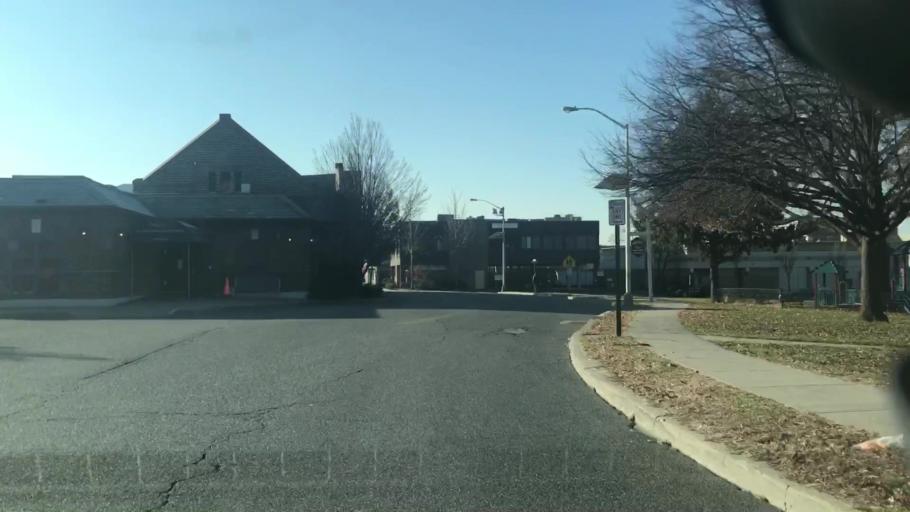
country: US
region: New Jersey
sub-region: Bergen County
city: Englewood
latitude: 40.8972
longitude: -73.9735
